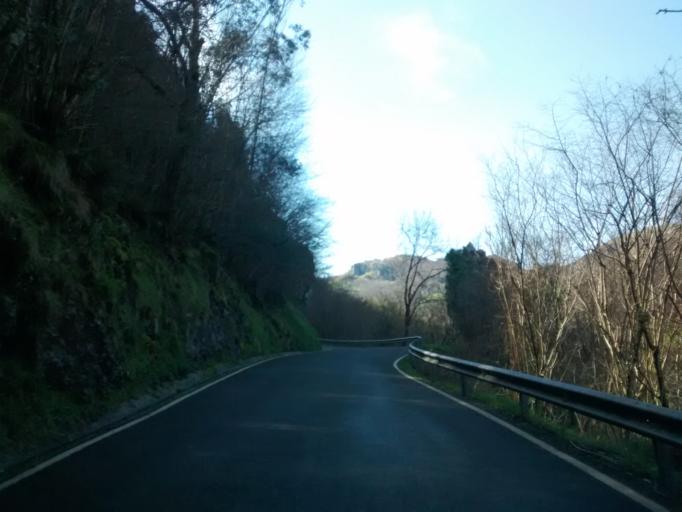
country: ES
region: Cantabria
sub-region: Provincia de Cantabria
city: Lierganes
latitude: 43.2797
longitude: -3.7006
